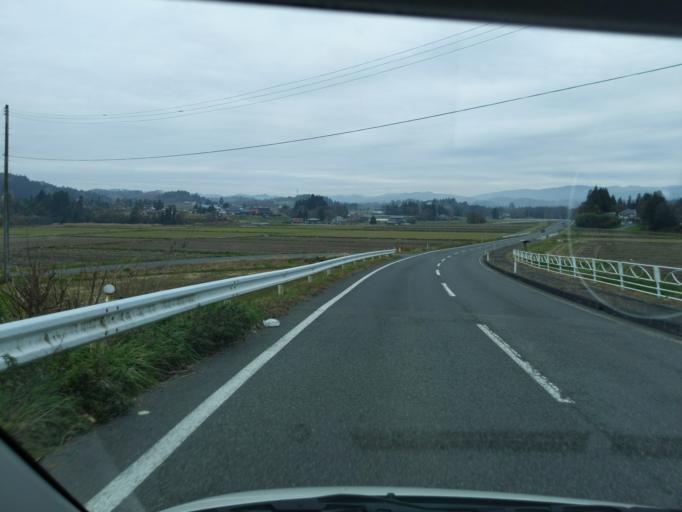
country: JP
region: Iwate
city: Mizusawa
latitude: 39.2119
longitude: 141.2201
